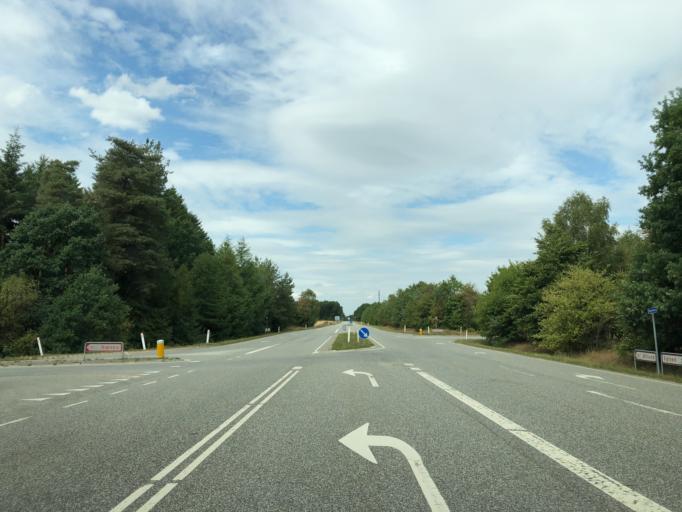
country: DK
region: South Denmark
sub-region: Vejle Kommune
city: Egtved
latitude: 55.6551
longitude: 9.2205
